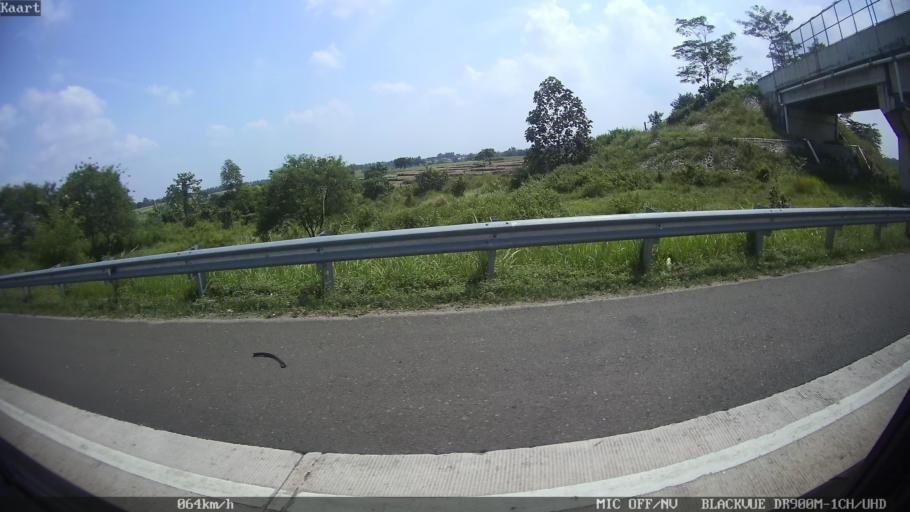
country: ID
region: Lampung
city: Kedaton
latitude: -5.3404
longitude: 105.3104
